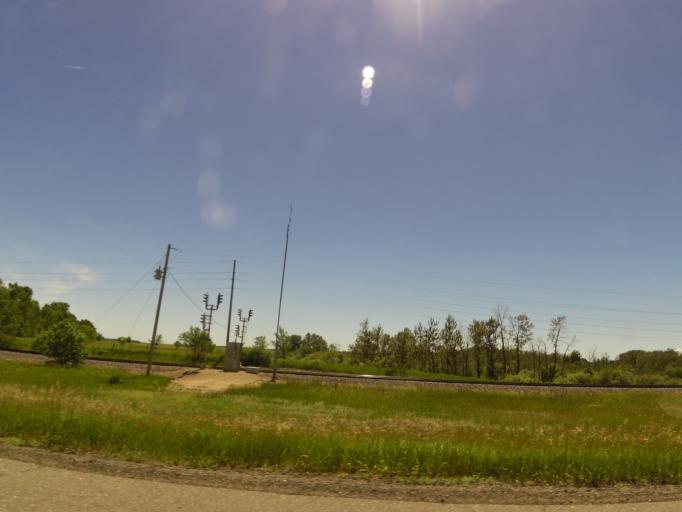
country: US
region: Minnesota
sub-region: Wadena County
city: Wadena
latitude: 46.4229
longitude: -95.0829
